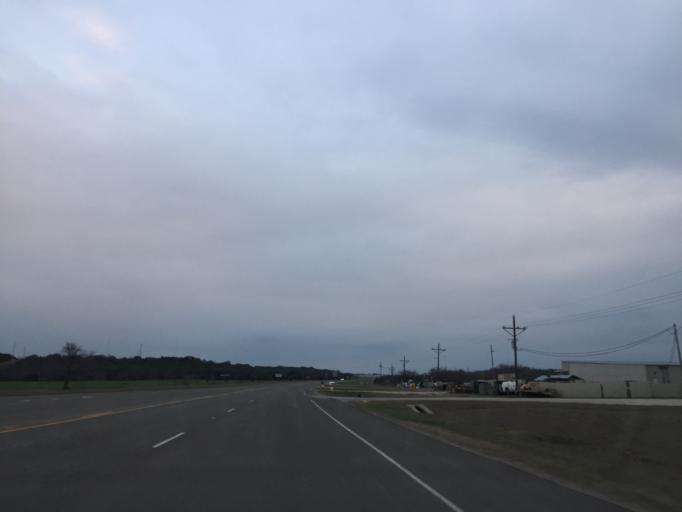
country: US
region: Texas
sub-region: Coryell County
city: Gatesville
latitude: 31.4704
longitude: -97.7185
